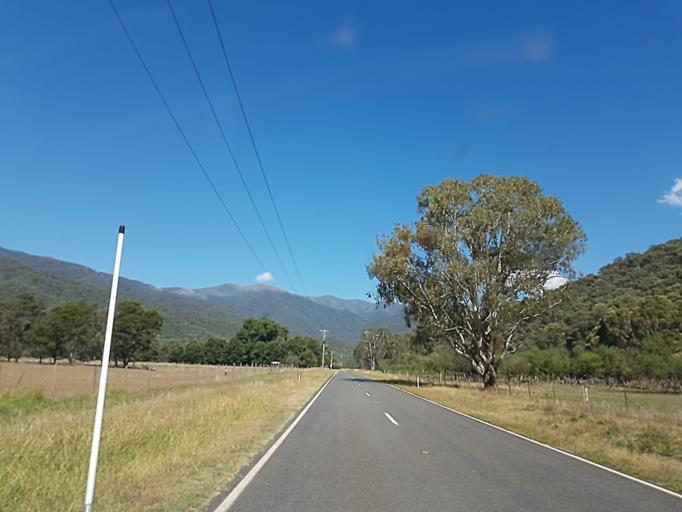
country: AU
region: Victoria
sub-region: Alpine
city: Mount Beauty
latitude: -36.8288
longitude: 147.0714
